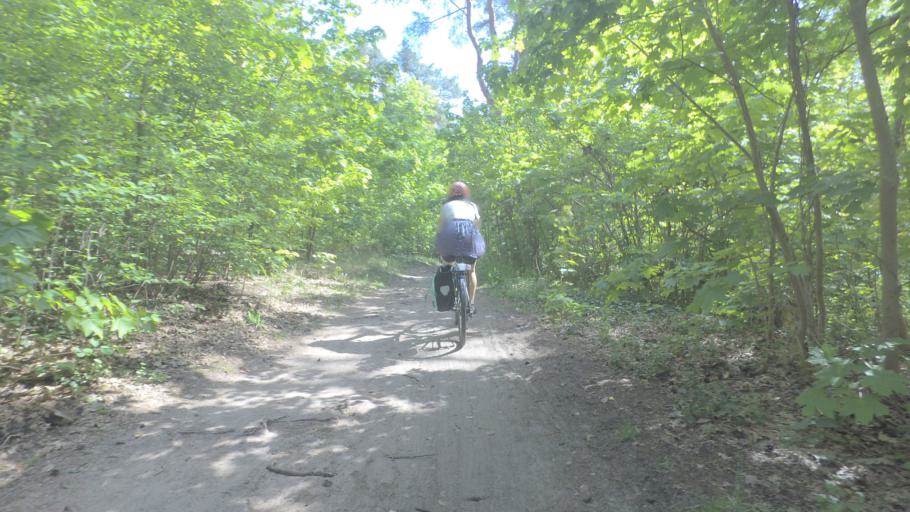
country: DE
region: Brandenburg
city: Erkner
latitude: 52.4251
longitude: 13.7637
